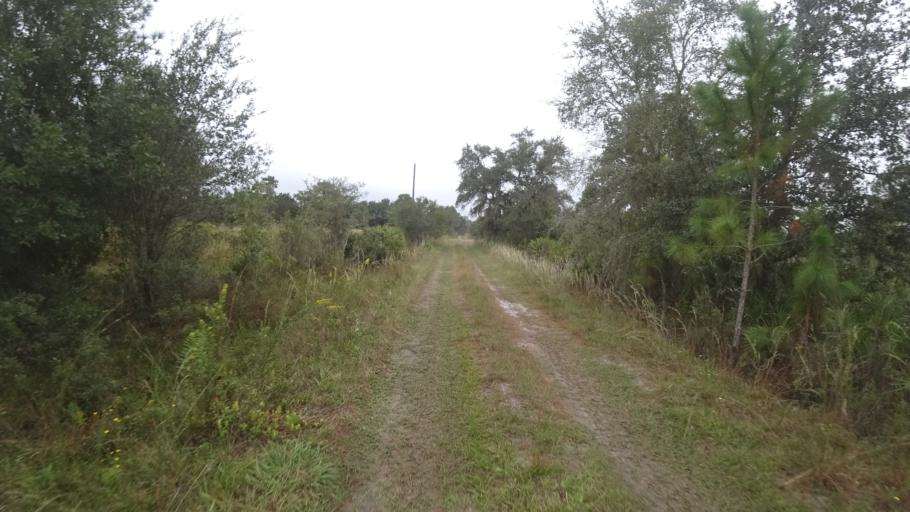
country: US
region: Florida
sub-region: Sarasota County
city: Warm Mineral Springs
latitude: 27.2753
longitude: -82.1252
